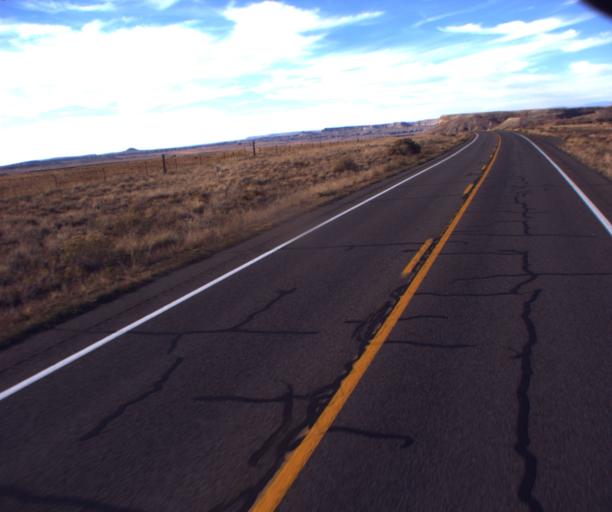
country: US
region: New Mexico
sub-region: San Juan County
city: Shiprock
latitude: 36.9099
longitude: -109.0723
